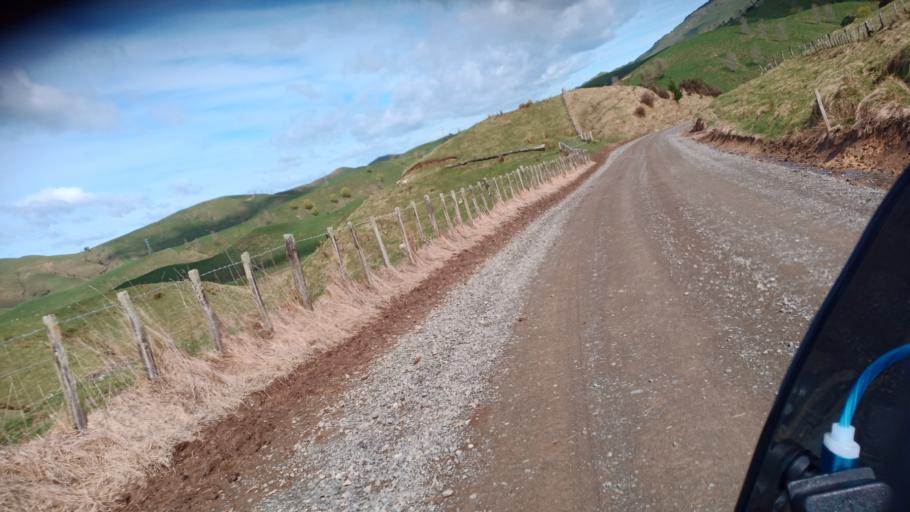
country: NZ
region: Hawke's Bay
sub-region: Wairoa District
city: Wairoa
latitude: -38.7382
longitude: 177.2954
